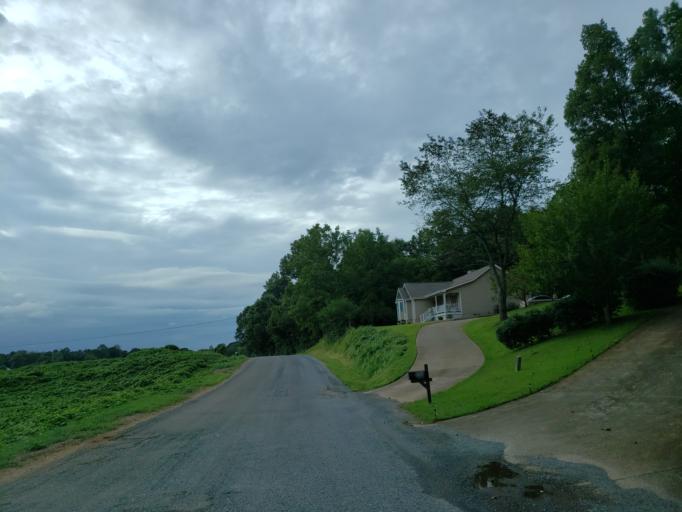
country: US
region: Georgia
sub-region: Pickens County
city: Jasper
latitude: 34.4721
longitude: -84.5101
